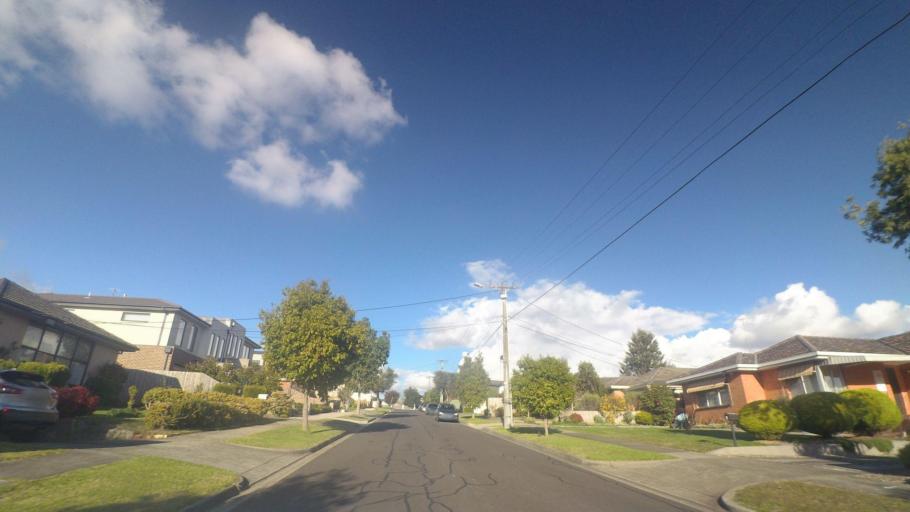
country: AU
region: Victoria
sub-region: Manningham
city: Templestowe Lower
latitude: -37.7808
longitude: 145.1095
